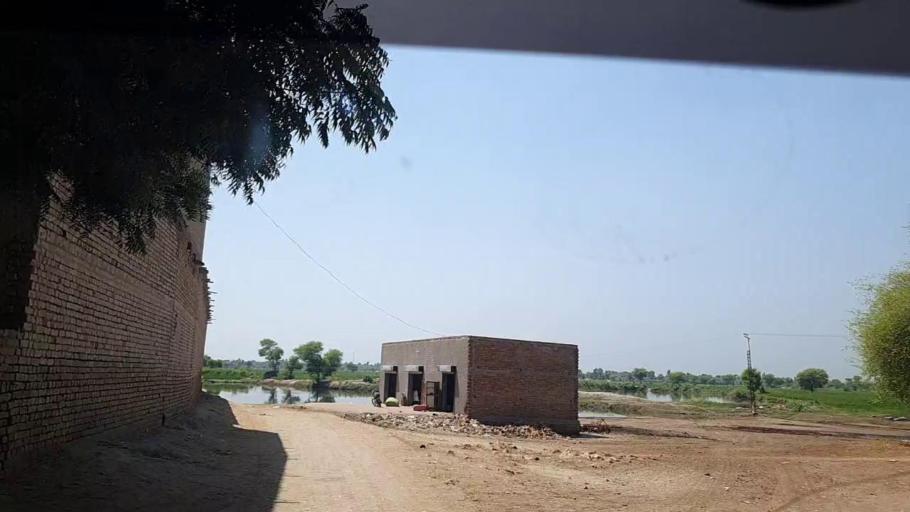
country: PK
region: Sindh
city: Ghauspur
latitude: 28.1666
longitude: 69.1262
